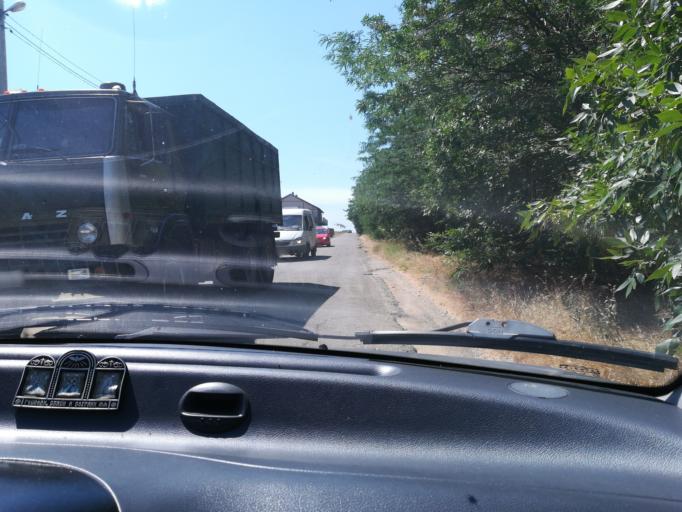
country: RU
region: Krasnodarskiy
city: Blagovetschenskaya
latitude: 45.0560
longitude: 37.1125
